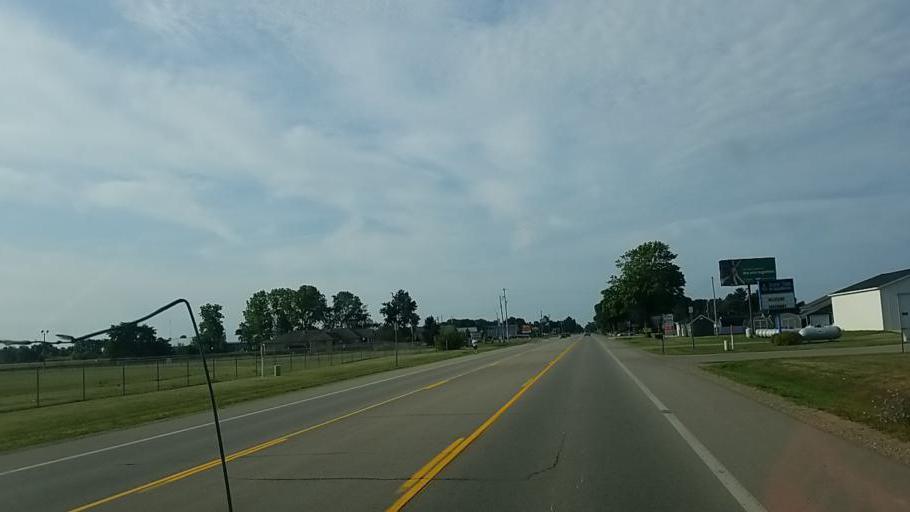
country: US
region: Michigan
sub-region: Ionia County
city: Ionia
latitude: 42.9379
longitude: -85.0748
